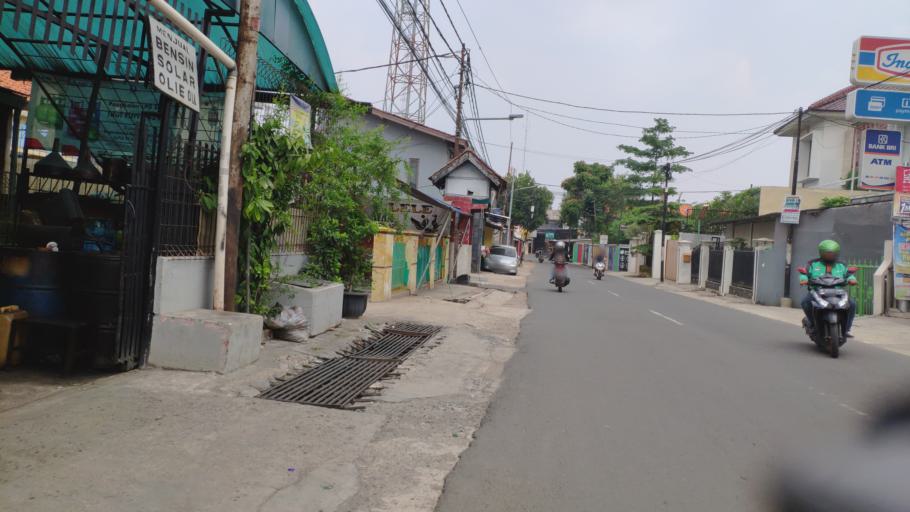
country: ID
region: West Java
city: Depok
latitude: -6.3450
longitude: 106.8294
